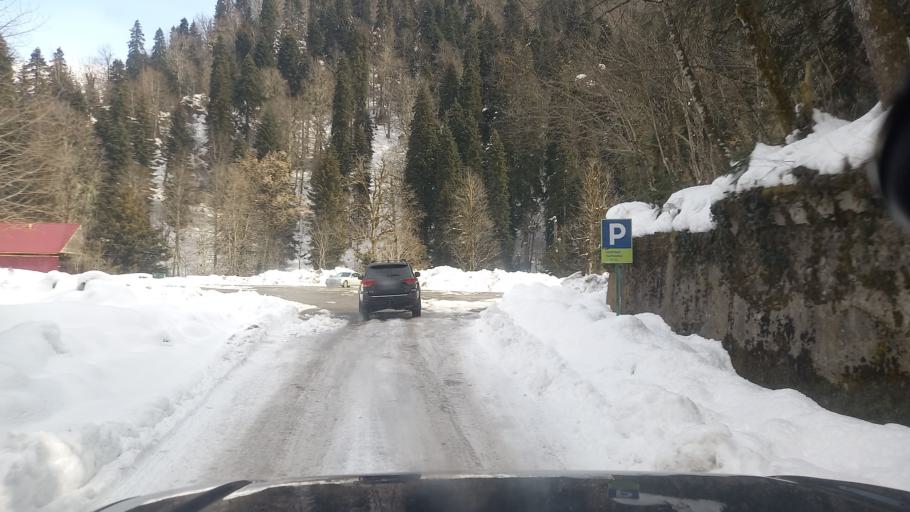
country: GE
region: Abkhazia
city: Gagra
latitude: 43.4748
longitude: 40.5391
